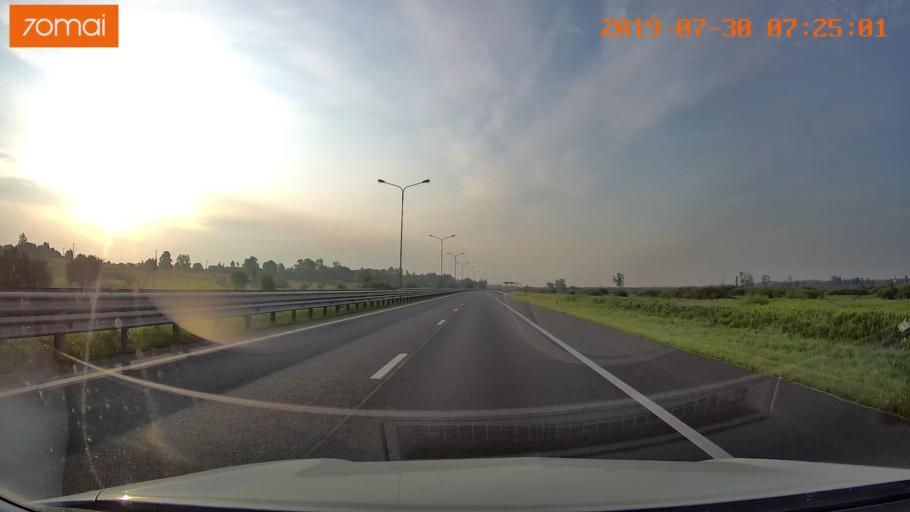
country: RU
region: Kaliningrad
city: Bol'shoe Isakovo
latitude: 54.6895
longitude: 20.8266
